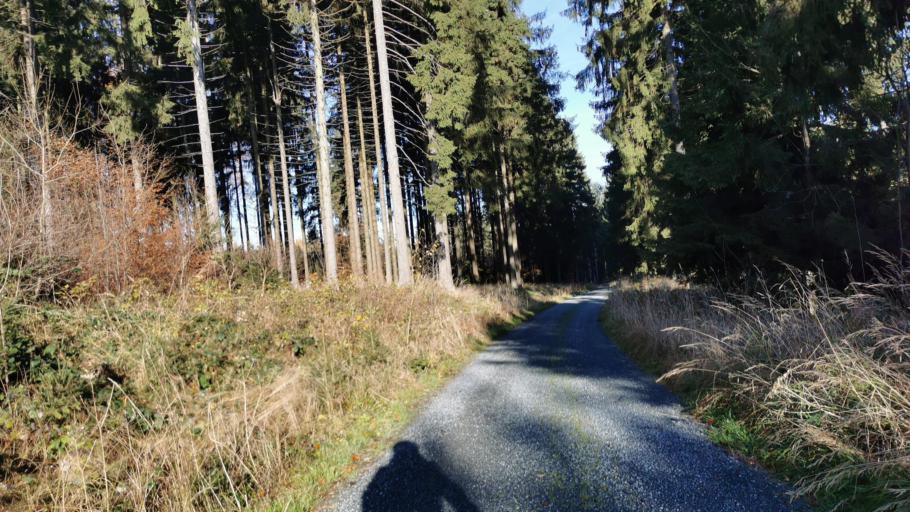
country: DE
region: Bavaria
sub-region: Upper Franconia
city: Ludwigsstadt
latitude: 50.4491
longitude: 11.3940
